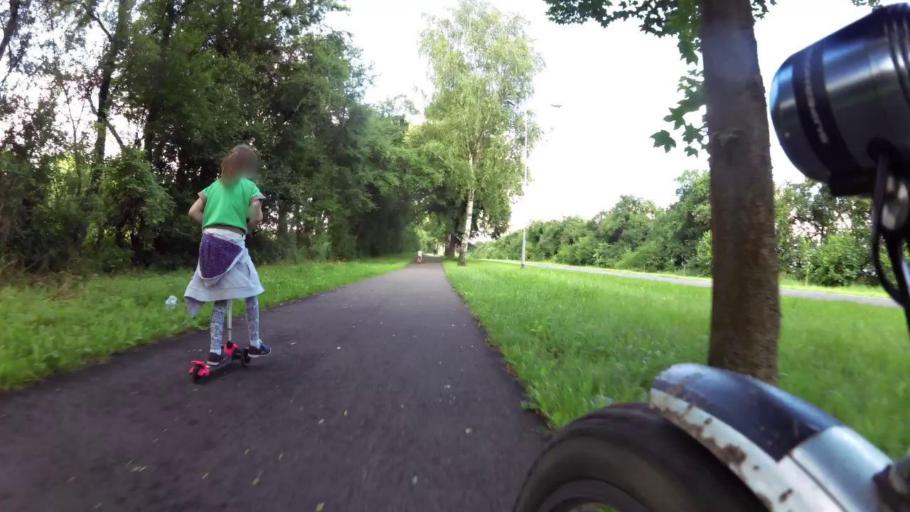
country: PL
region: West Pomeranian Voivodeship
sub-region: Powiat swidwinski
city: Swidwin
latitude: 53.7761
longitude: 15.7987
